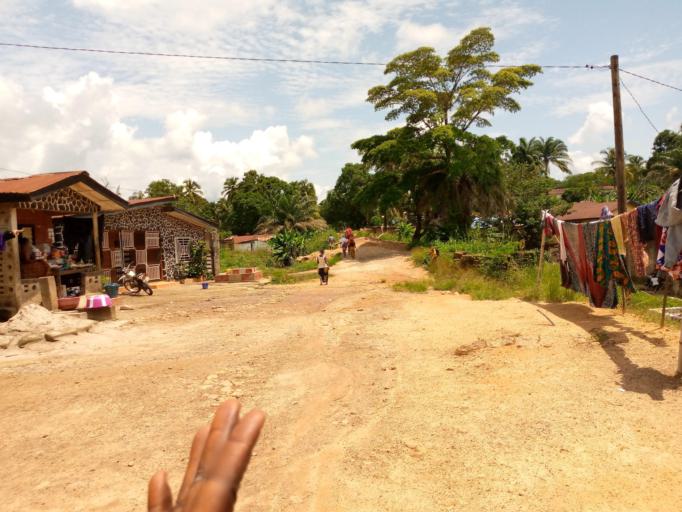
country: SL
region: Northern Province
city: Magburaka
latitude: 8.7266
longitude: -11.9446
